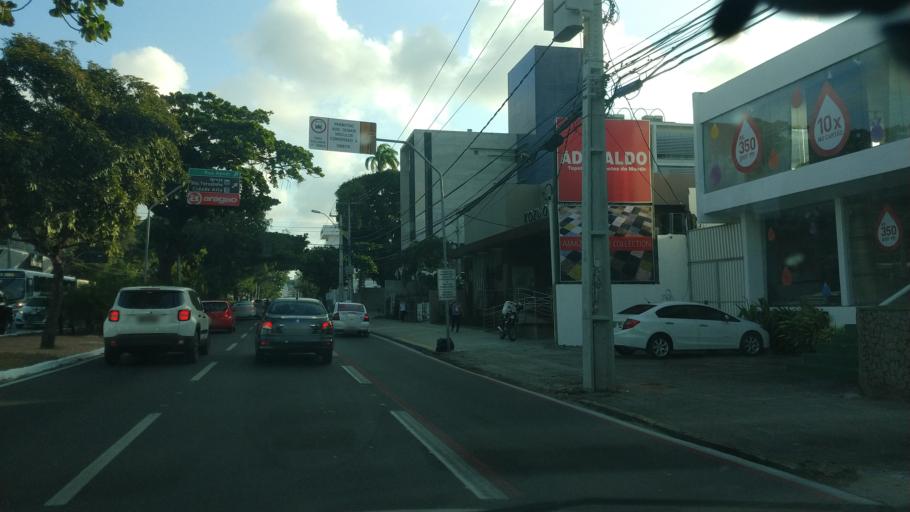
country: BR
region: Rio Grande do Norte
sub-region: Natal
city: Natal
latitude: -5.7912
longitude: -35.1972
